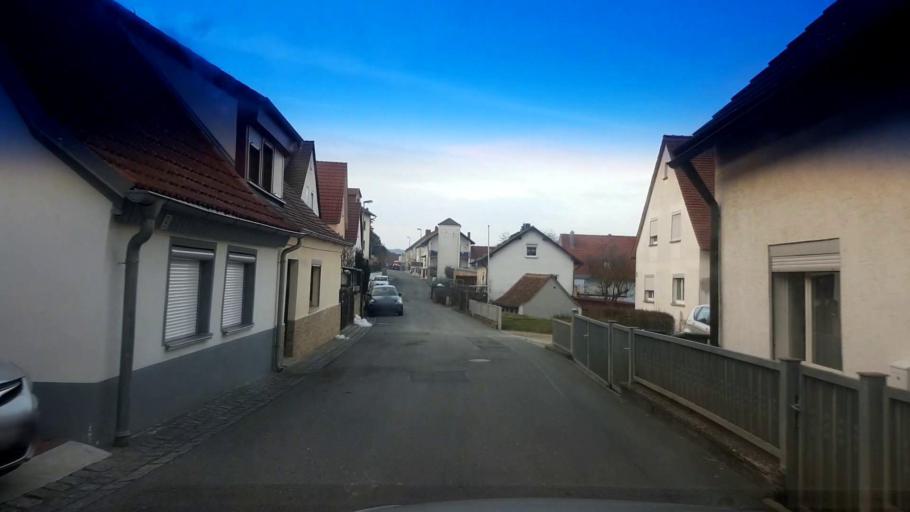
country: DE
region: Bavaria
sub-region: Upper Franconia
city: Hirschaid
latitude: 49.8067
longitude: 10.9840
